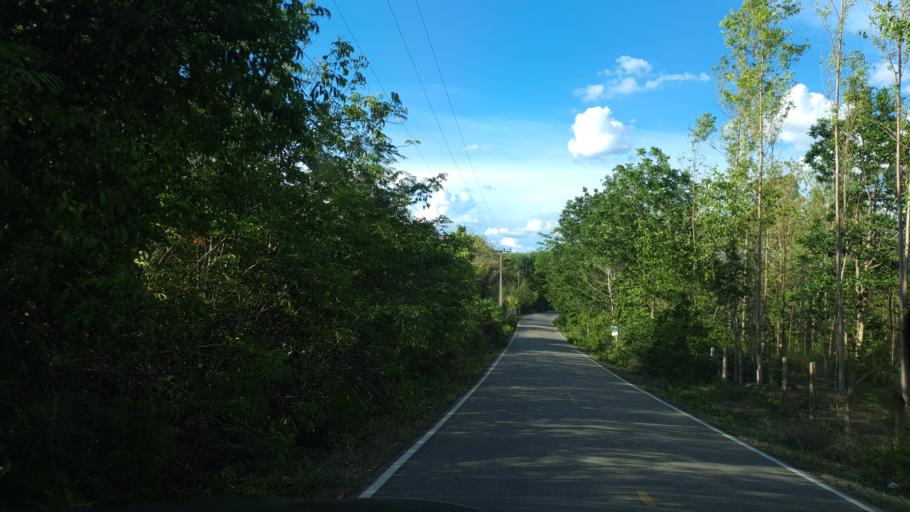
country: TH
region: Lampang
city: Sop Prap
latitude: 17.8794
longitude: 99.3102
